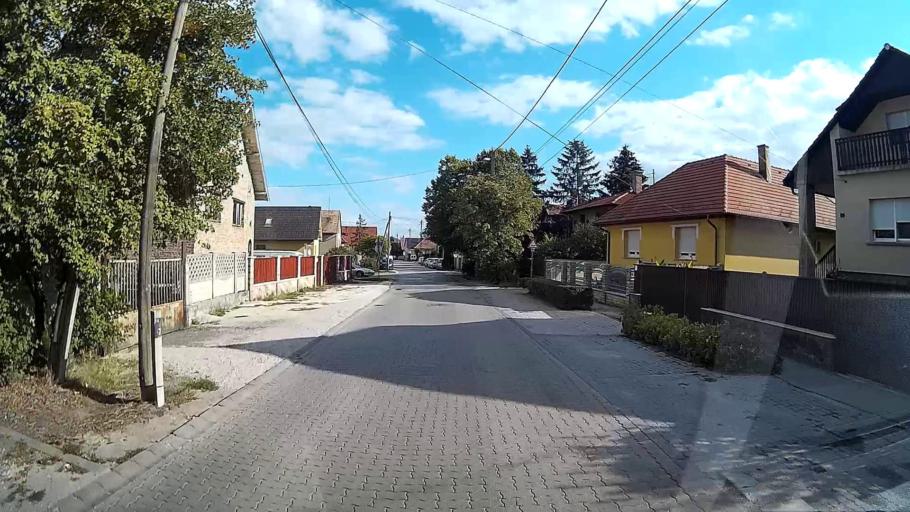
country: HU
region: Pest
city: Pilisvorosvar
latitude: 47.6254
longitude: 18.9010
